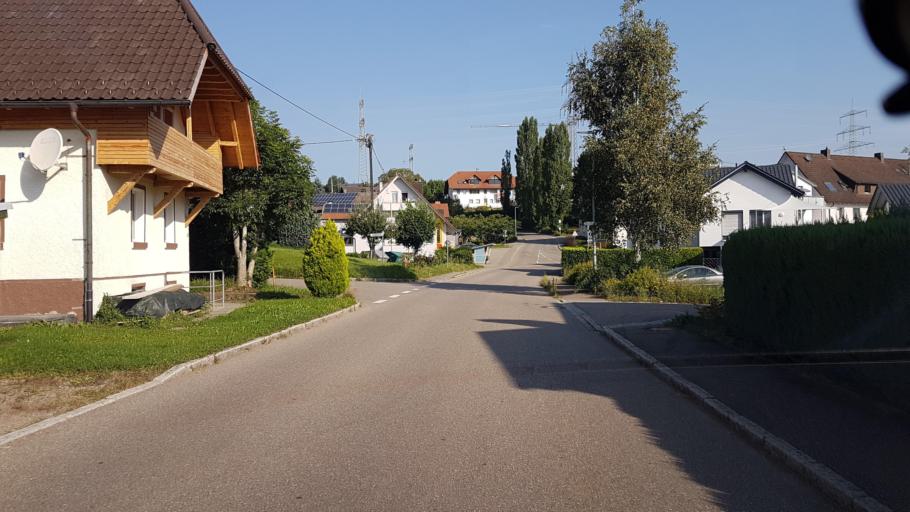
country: DE
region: Baden-Wuerttemberg
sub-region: Freiburg Region
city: Albbruck
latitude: 47.6124
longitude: 8.1128
